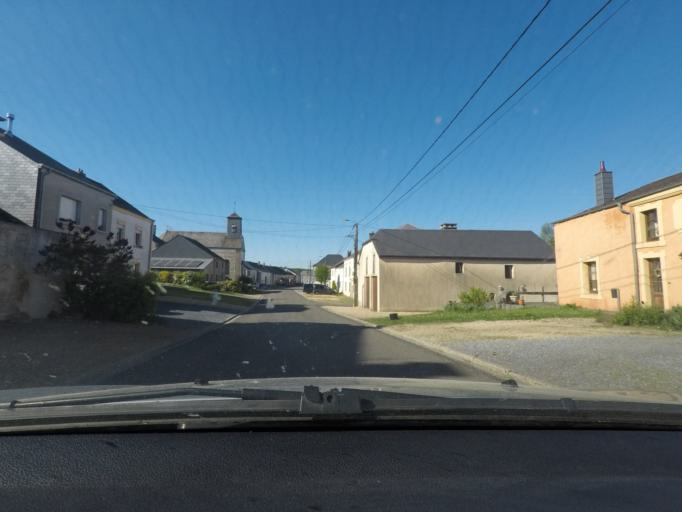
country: BE
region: Wallonia
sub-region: Province du Luxembourg
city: Tintigny
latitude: 49.7055
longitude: 5.4571
